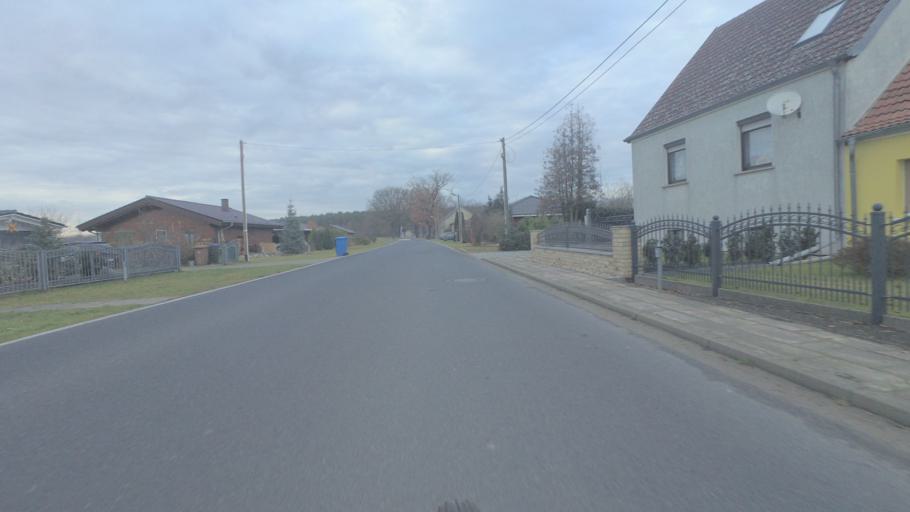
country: DE
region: Brandenburg
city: Sperenberg
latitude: 52.1901
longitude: 13.3224
